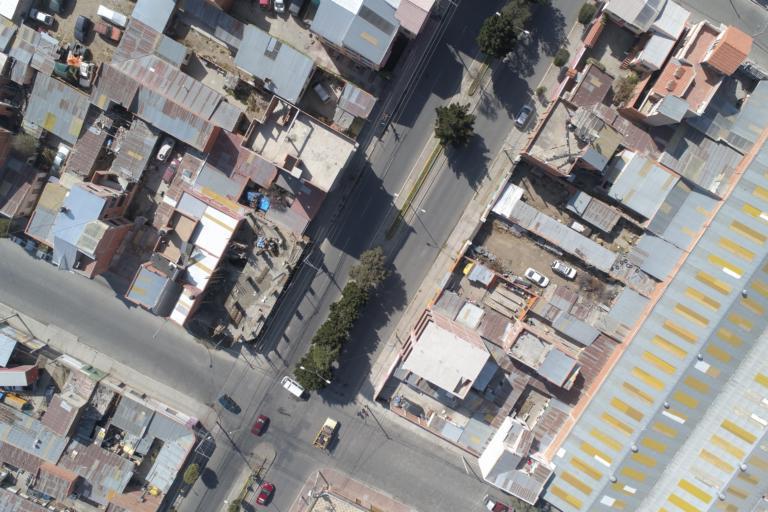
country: BO
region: La Paz
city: La Paz
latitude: -16.5283
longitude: -68.1470
